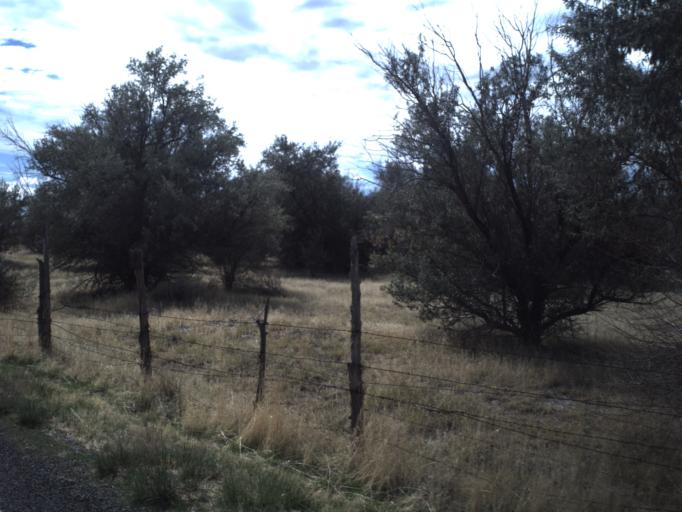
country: US
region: Utah
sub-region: Millard County
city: Fillmore
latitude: 39.0856
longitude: -112.4099
